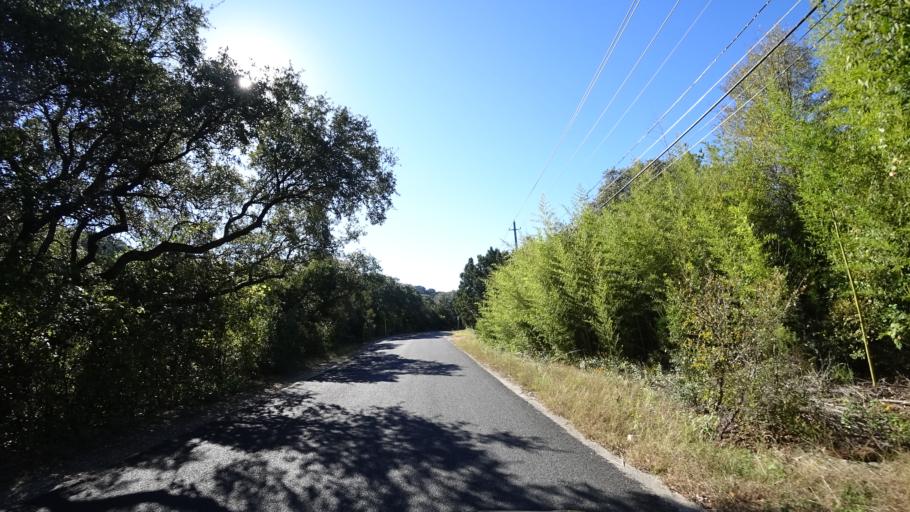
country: US
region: Texas
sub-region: Travis County
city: West Lake Hills
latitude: 30.3688
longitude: -97.7860
